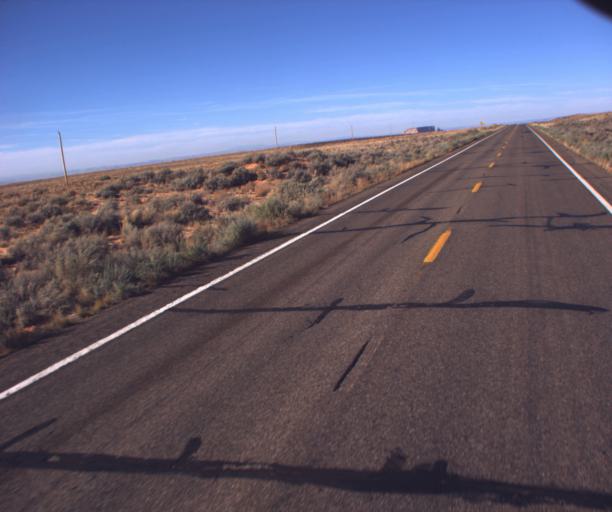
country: US
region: Arizona
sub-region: Coconino County
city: LeChee
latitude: 36.7497
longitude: -111.2848
